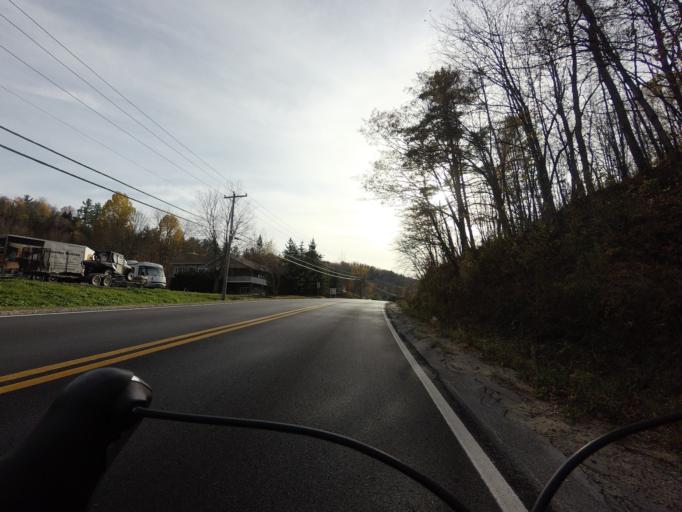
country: CA
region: Quebec
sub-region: Outaouais
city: Val-des-Monts
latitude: 45.6620
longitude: -75.7367
